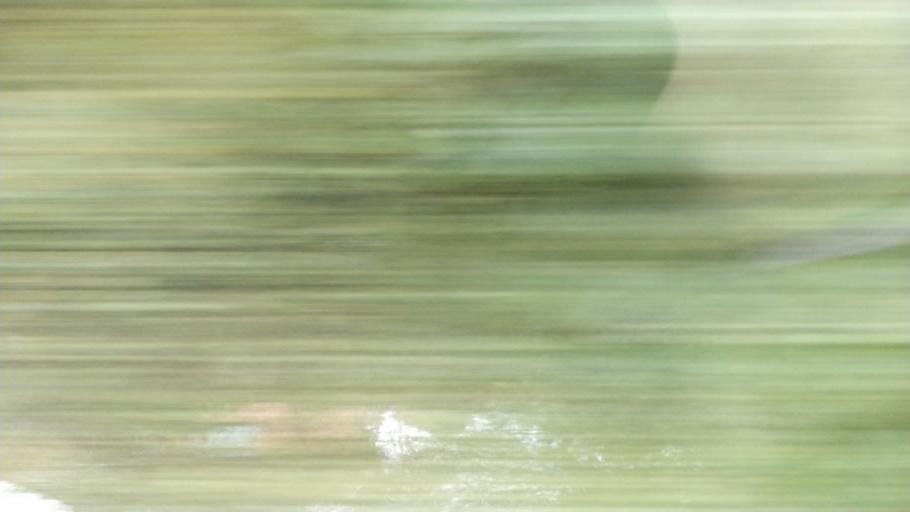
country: GB
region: England
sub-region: Borough of Bolton
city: Westhoughton
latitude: 53.5415
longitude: -2.5259
